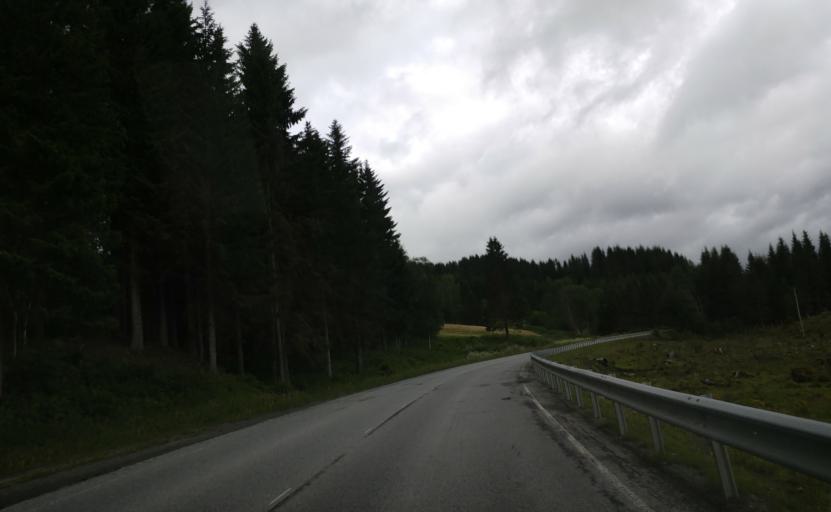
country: NO
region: Sor-Trondelag
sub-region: Selbu
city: Mebonden
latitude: 63.2974
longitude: 11.0760
